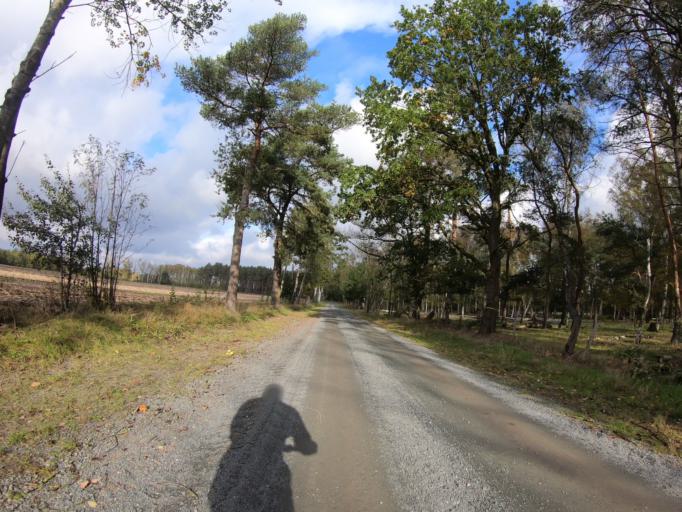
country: DE
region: Lower Saxony
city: Wesendorf
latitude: 52.5615
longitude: 10.5586
